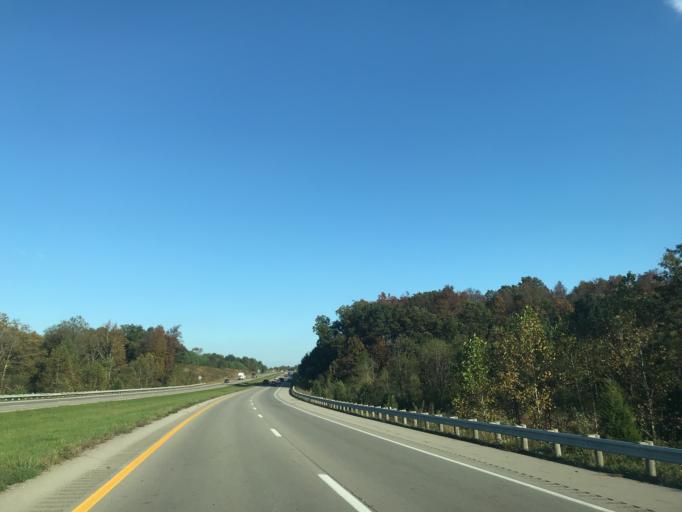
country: US
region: Ohio
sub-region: Pike County
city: Piketon
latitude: 39.0537
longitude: -82.9614
